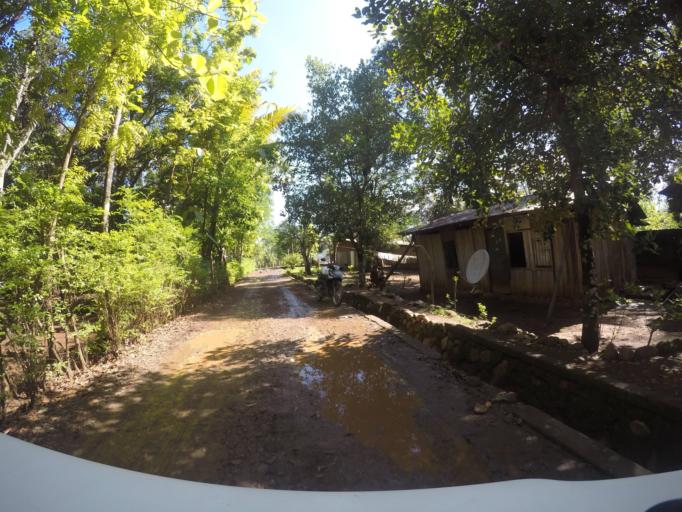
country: TL
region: Bobonaro
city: Maliana
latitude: -8.9903
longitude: 125.2073
